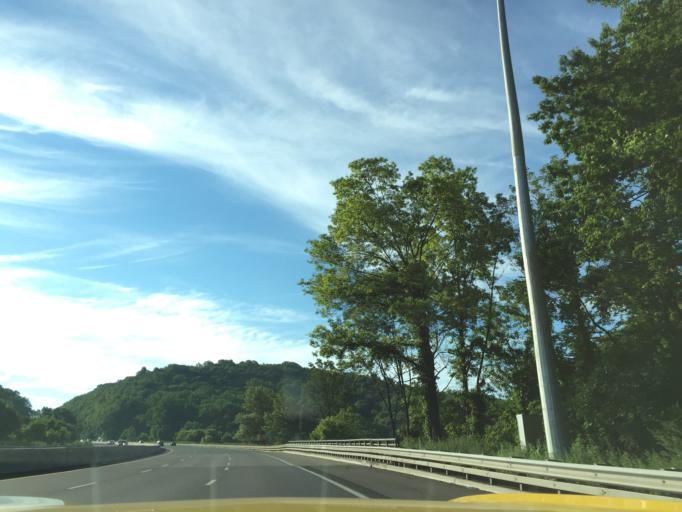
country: US
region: New Jersey
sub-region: Hunterdon County
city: Hampton
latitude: 40.6516
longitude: -75.0354
